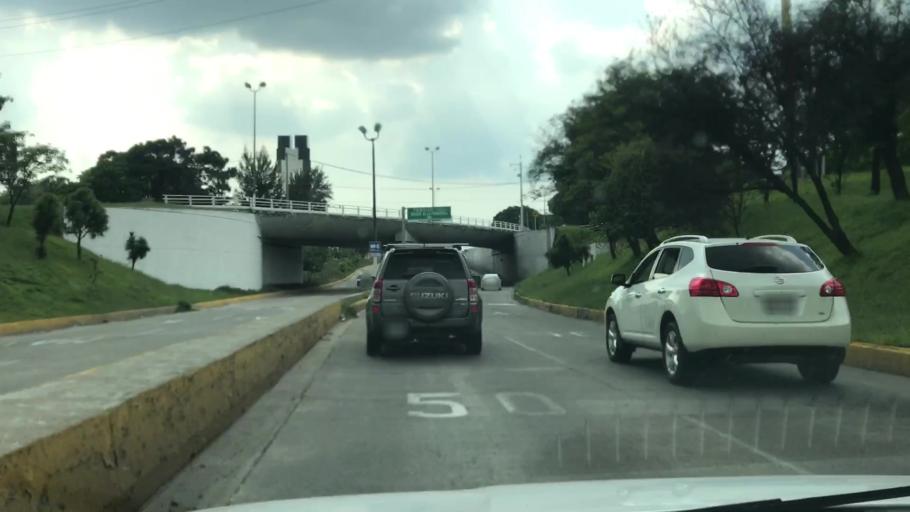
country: MX
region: Jalisco
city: Guadalajara
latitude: 20.6773
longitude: -103.4138
